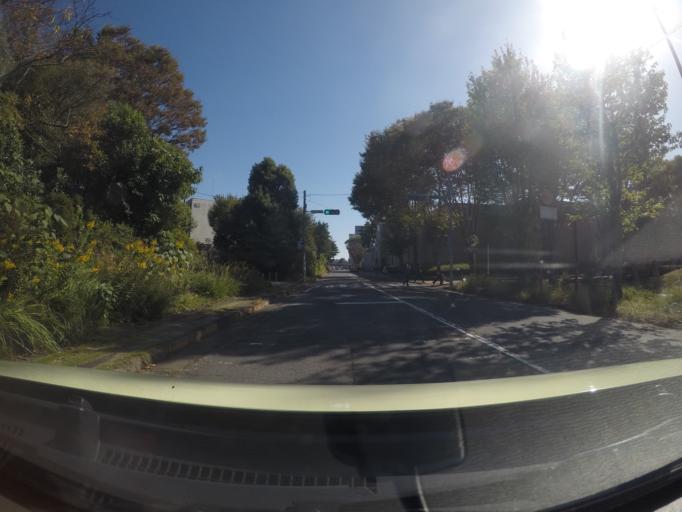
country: JP
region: Ibaraki
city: Naka
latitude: 36.0846
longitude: 140.1120
